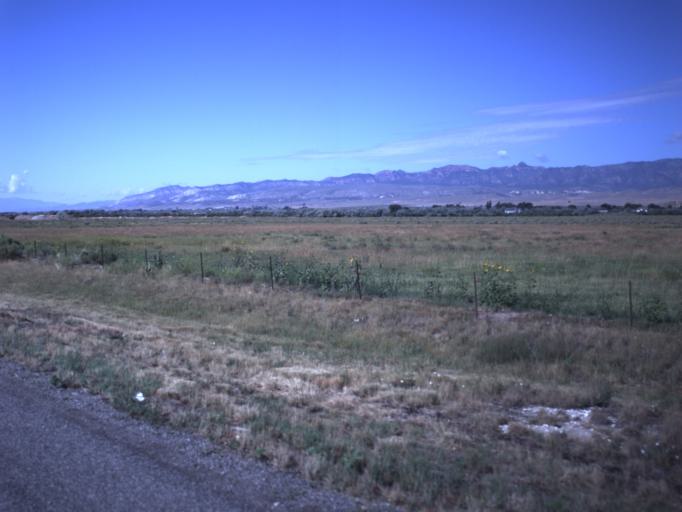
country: US
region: Utah
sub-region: Sevier County
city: Salina
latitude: 39.0032
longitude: -111.8397
